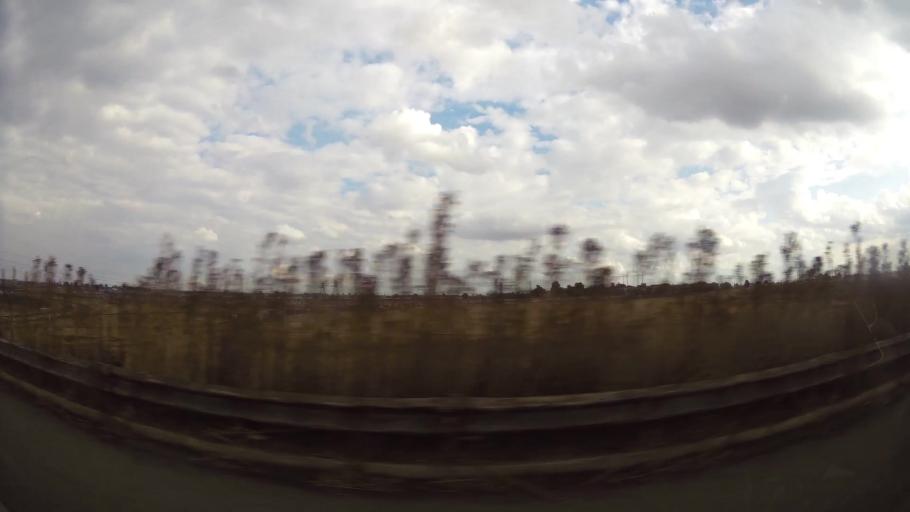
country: ZA
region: Orange Free State
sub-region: Fezile Dabi District Municipality
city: Sasolburg
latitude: -26.8332
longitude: 27.8617
